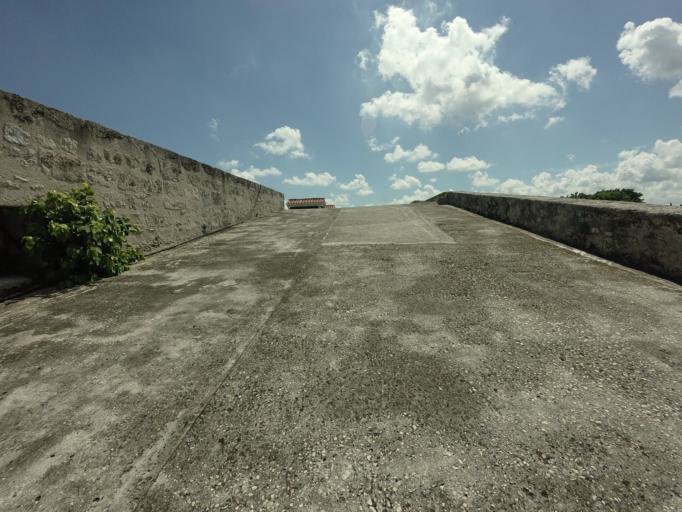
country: CU
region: La Habana
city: Centro Habana
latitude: 23.1482
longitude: -82.3520
